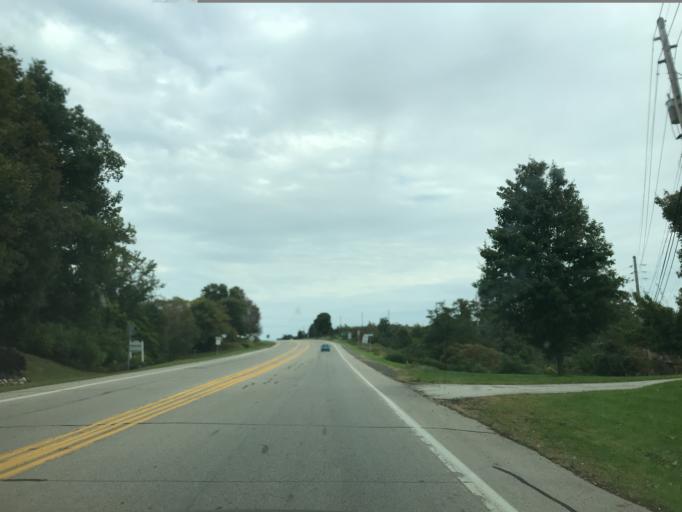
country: US
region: Pennsylvania
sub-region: Erie County
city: North East
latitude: 42.2191
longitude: -79.8232
